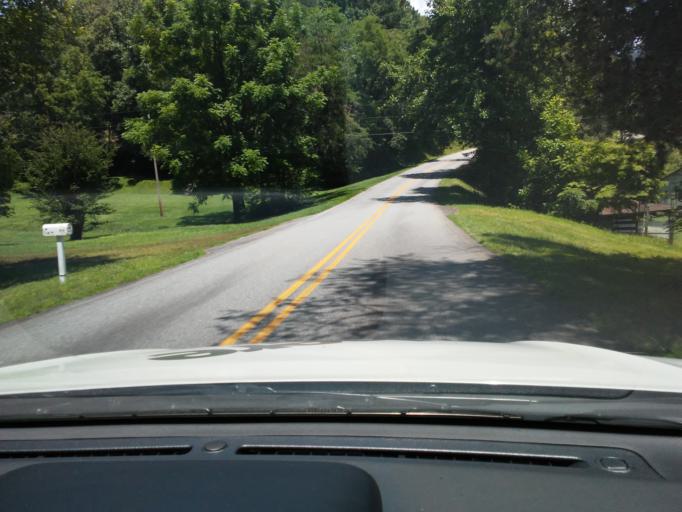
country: US
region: Georgia
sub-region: Towns County
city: Hiawassee
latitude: 34.8692
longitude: -83.7342
